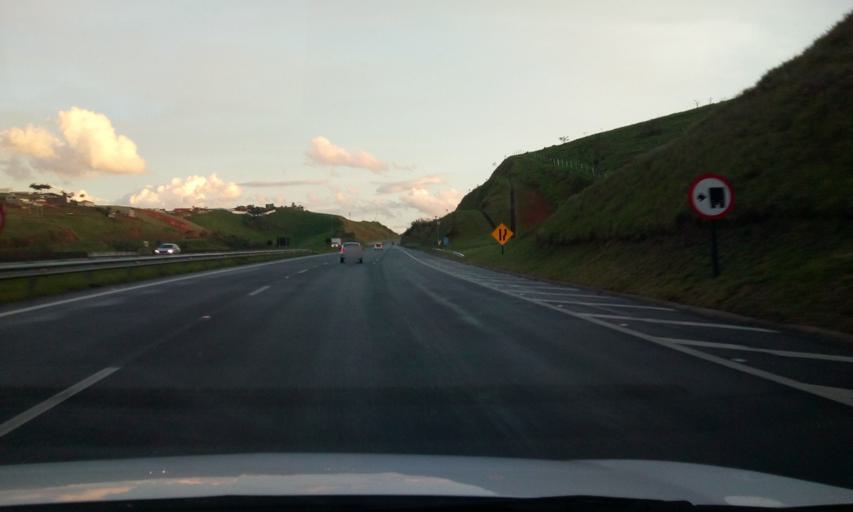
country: BR
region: Sao Paulo
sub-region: Santa Isabel
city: Santa Isabel
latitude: -23.2233
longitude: -46.1375
